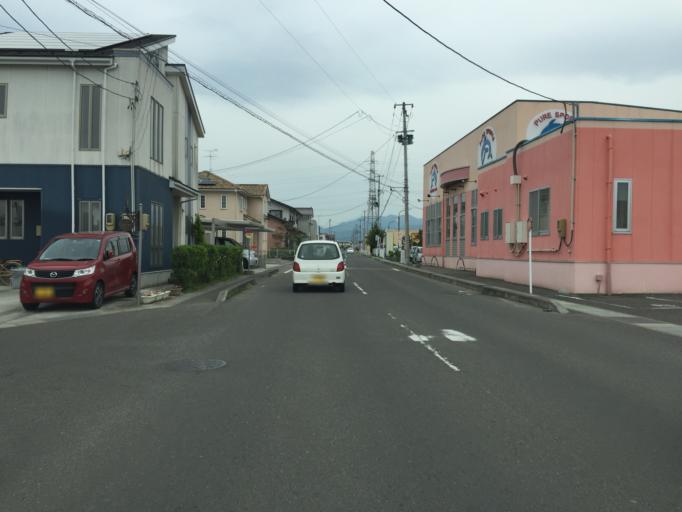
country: JP
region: Fukushima
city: Fukushima-shi
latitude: 37.7927
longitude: 140.4501
